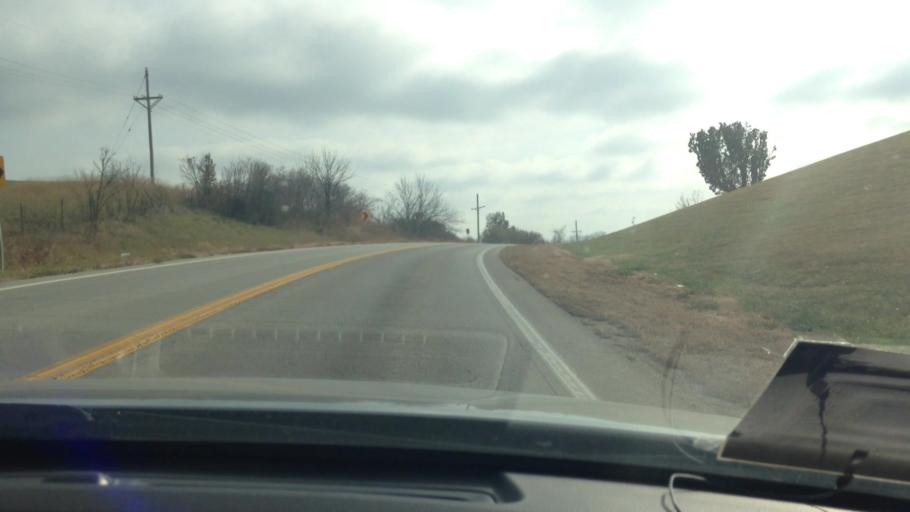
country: US
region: Missouri
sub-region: Platte County
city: Weatherby Lake
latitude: 39.2320
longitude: -94.7823
